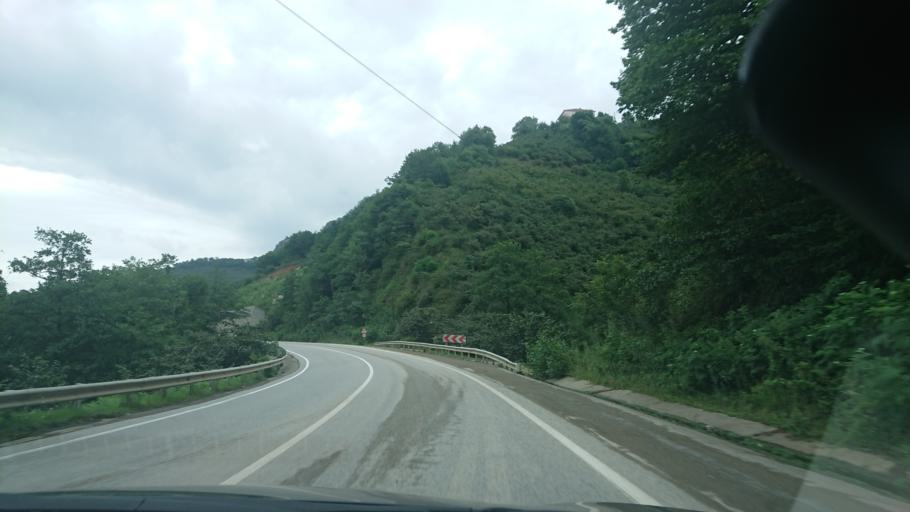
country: TR
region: Giresun
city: Tirebolu
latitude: 40.9447
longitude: 38.8616
